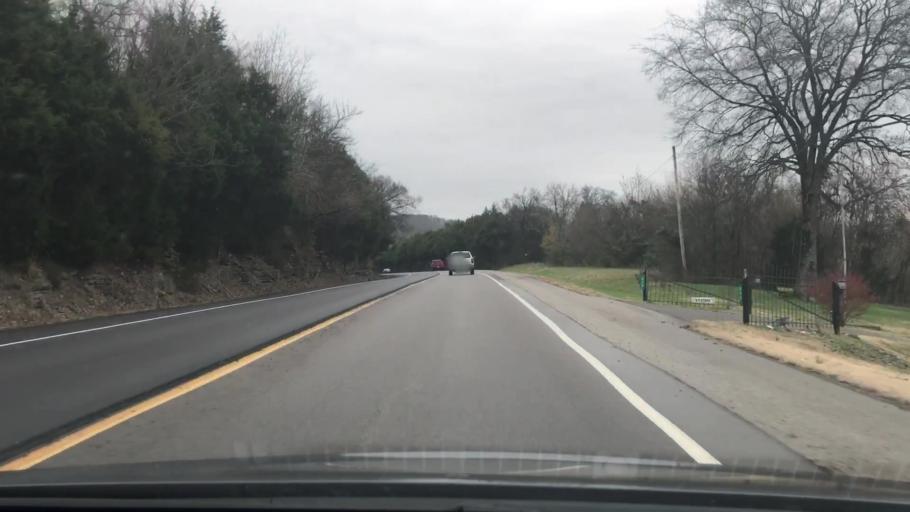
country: US
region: Tennessee
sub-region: Smith County
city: Carthage
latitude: 36.3282
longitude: -86.0224
